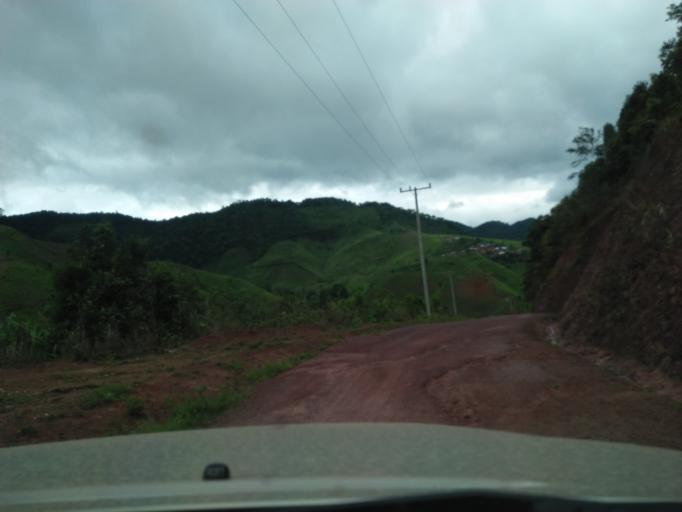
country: TH
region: Nan
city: Bo Kluea
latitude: 19.3768
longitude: 101.2150
